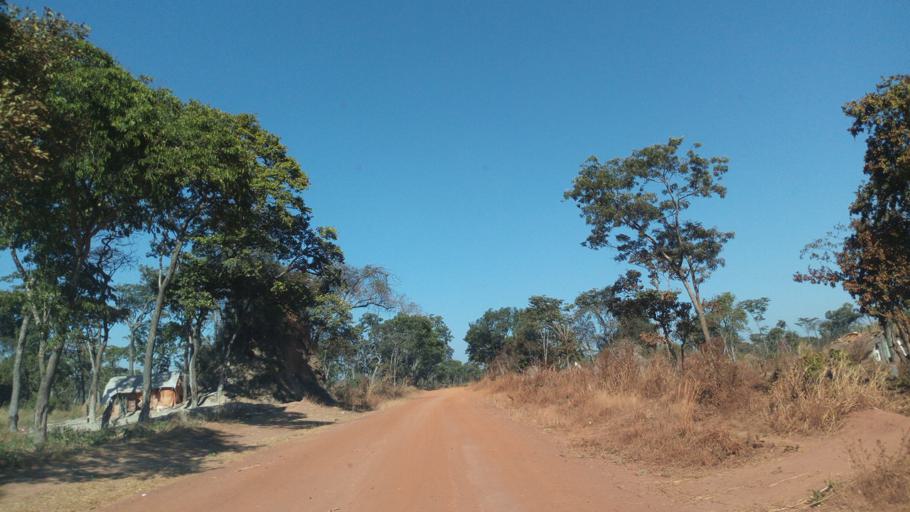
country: ZM
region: Luapula
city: Mwense
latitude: -10.6824
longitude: 28.4006
